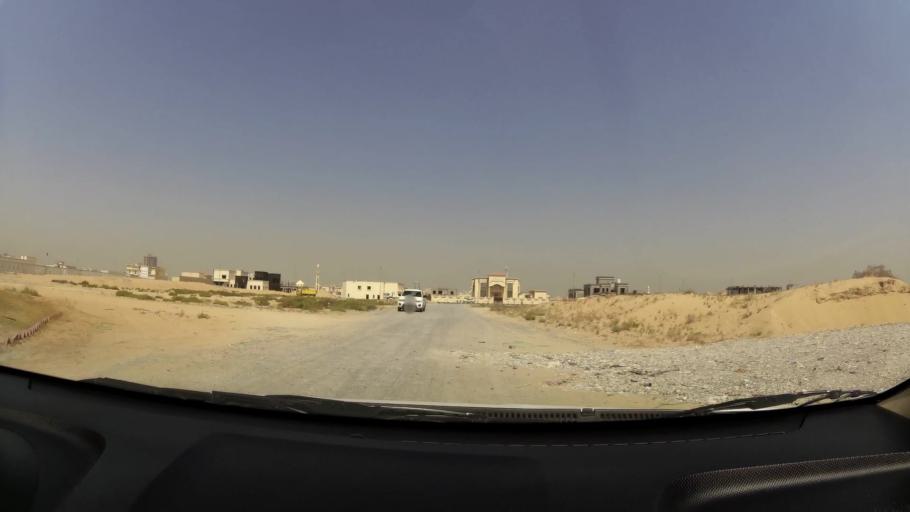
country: AE
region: Ajman
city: Ajman
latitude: 25.4051
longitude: 55.5276
